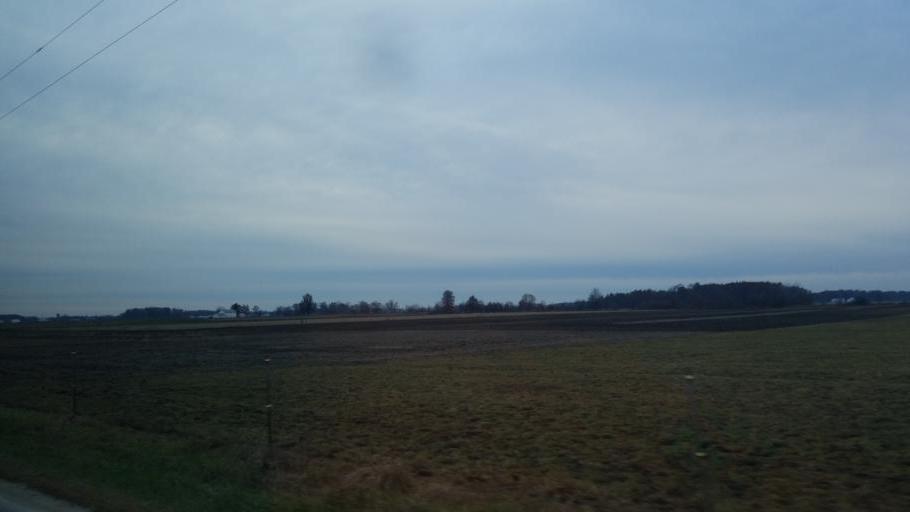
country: US
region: Indiana
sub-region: Adams County
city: Berne
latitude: 40.7127
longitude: -84.8796
